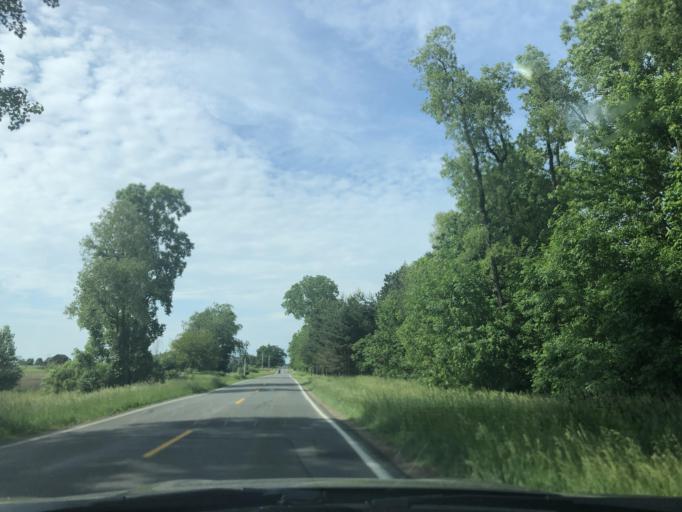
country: US
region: Michigan
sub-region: Clinton County
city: Bath
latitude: 42.8168
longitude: -84.4837
